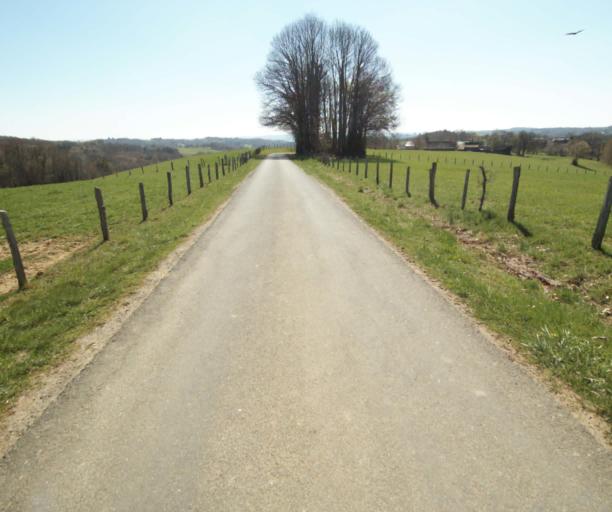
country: FR
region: Limousin
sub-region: Departement de la Correze
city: Saint-Clement
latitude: 45.3294
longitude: 1.7107
